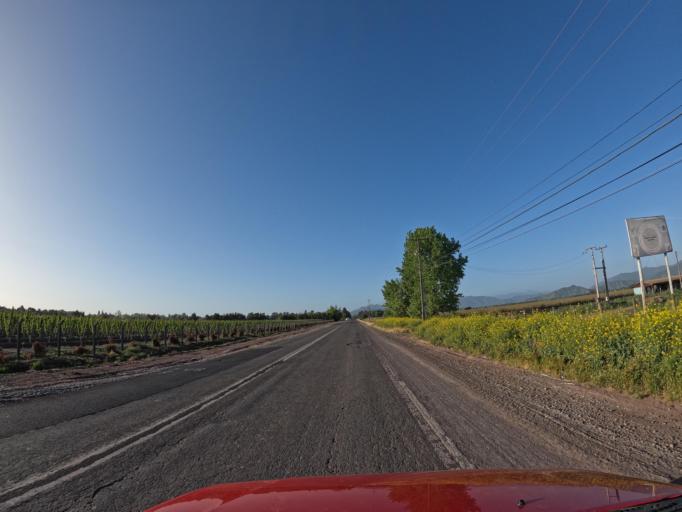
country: CL
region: O'Higgins
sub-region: Provincia de Colchagua
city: Santa Cruz
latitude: -34.5034
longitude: -71.3627
